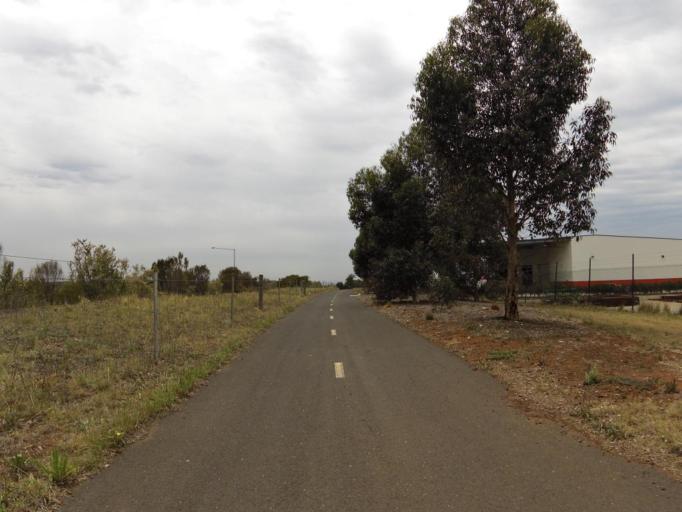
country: AU
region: Victoria
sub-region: Brimbank
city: Derrimut
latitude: -37.7991
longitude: 144.7738
